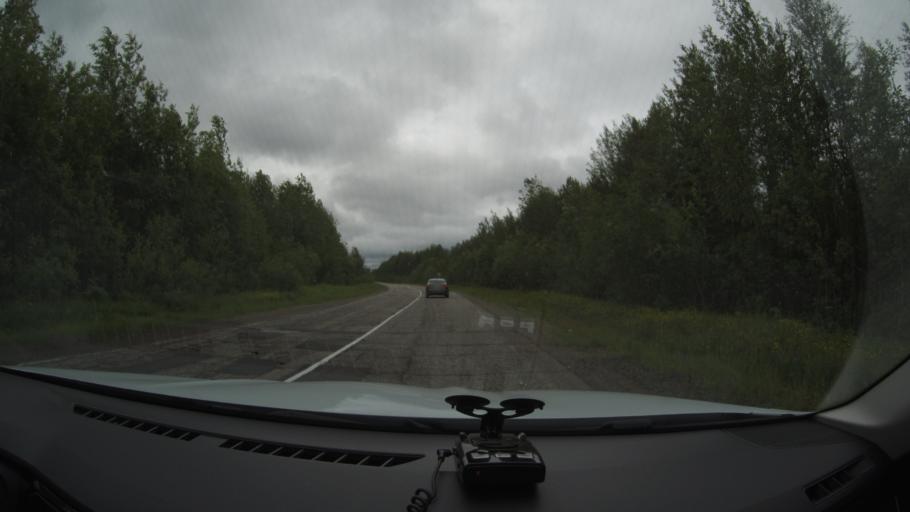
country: RU
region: Komi Republic
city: Nizhniy Odes
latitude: 63.6124
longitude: 54.5749
